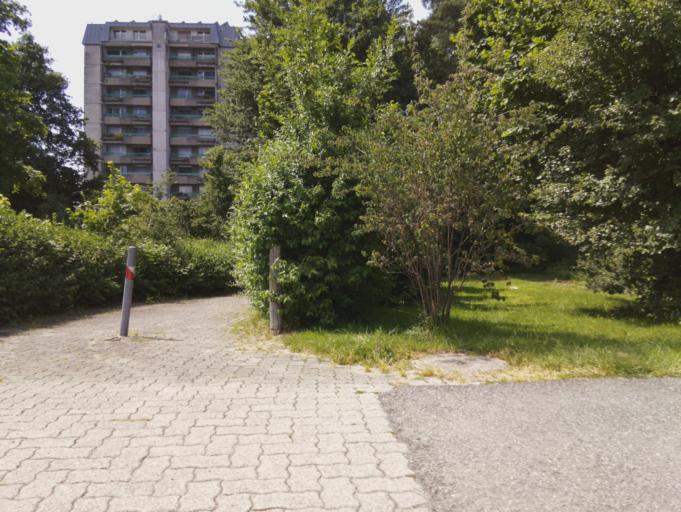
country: CH
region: Schwyz
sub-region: Bezirk March
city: Lachen
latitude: 47.1977
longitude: 8.8594
